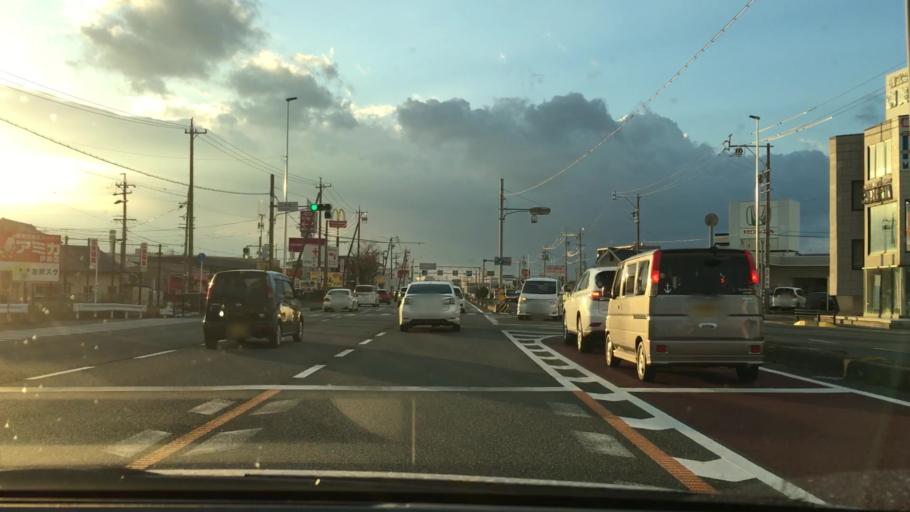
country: JP
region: Mie
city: Ise
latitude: 34.5069
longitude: 136.7260
